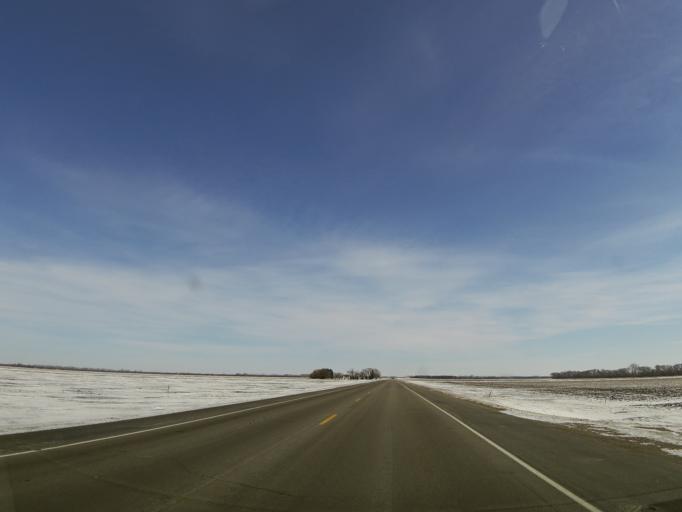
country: US
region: North Dakota
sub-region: Walsh County
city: Grafton
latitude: 48.4121
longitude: -97.2185
